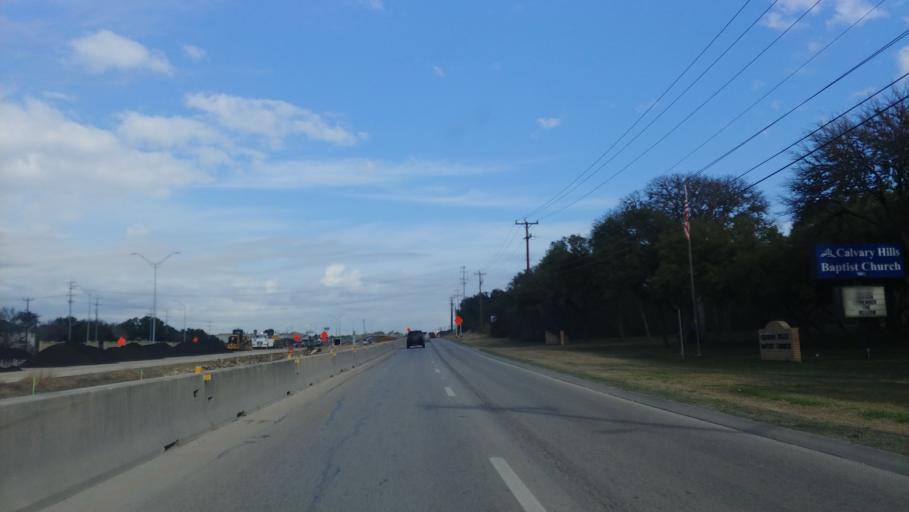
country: US
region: Texas
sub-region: Bexar County
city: Leon Valley
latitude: 29.4412
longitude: -98.7109
